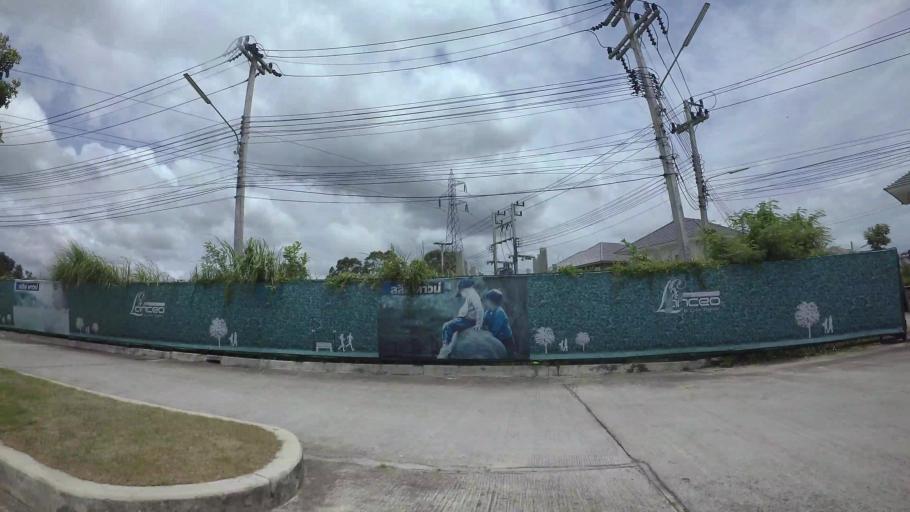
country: TH
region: Chon Buri
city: Si Racha
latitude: 13.1706
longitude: 100.9737
